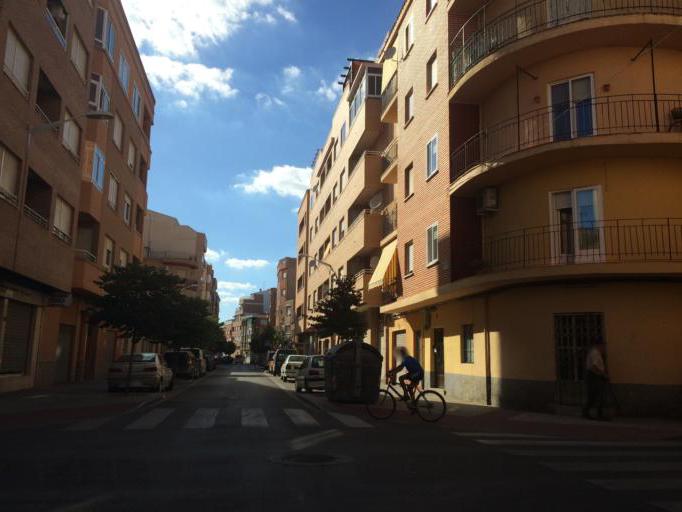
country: ES
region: Castille-La Mancha
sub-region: Provincia de Albacete
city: Albacete
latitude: 38.9958
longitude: -1.8743
